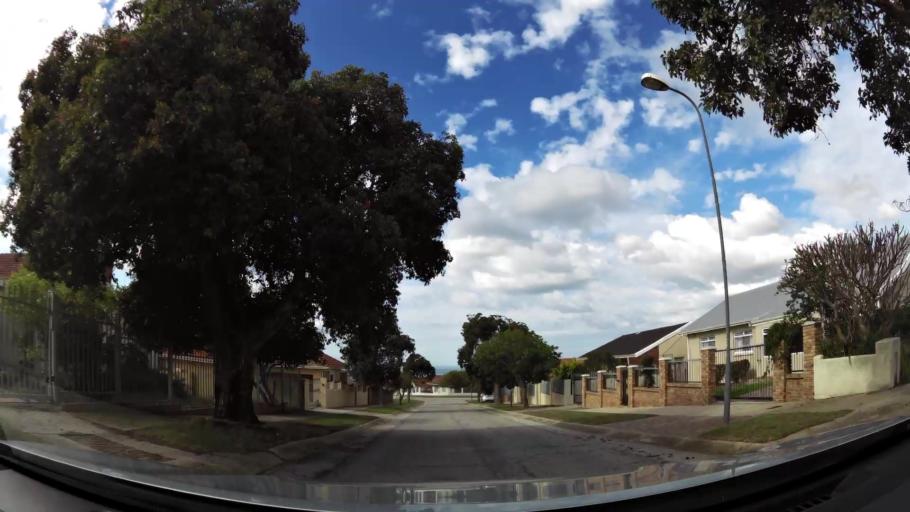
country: ZA
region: Eastern Cape
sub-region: Nelson Mandela Bay Metropolitan Municipality
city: Port Elizabeth
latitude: -33.9436
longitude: 25.5844
